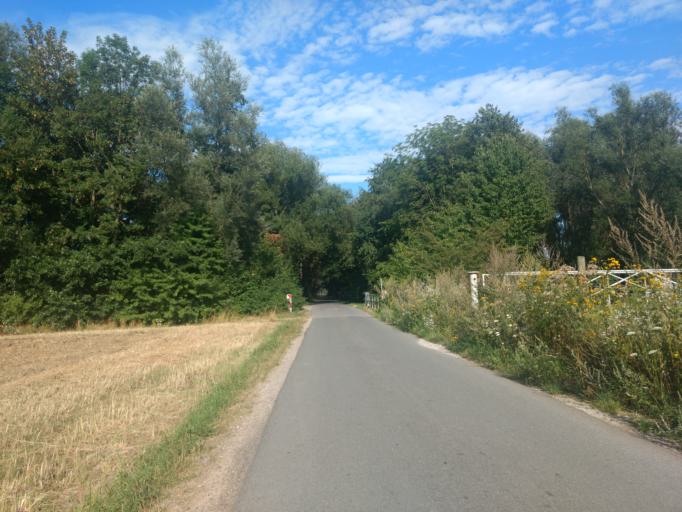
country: DE
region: North Rhine-Westphalia
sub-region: Regierungsbezirk Detmold
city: Hovelhof
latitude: 51.7476
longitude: 8.6401
